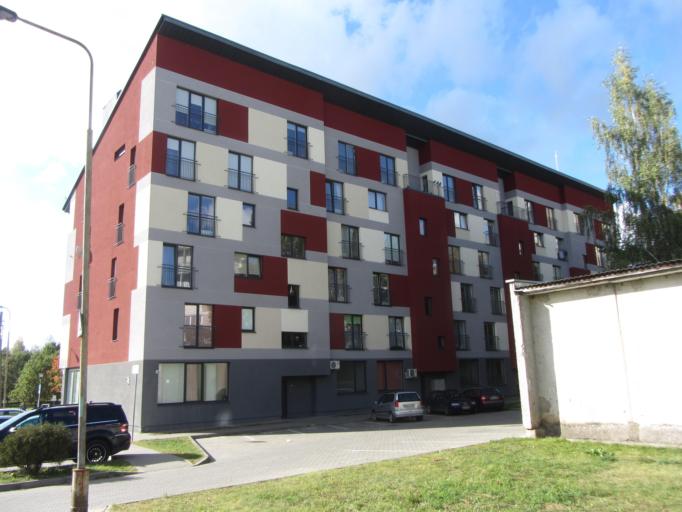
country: LT
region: Utenos apskritis
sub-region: Utena
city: Utena
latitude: 55.4954
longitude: 25.6151
